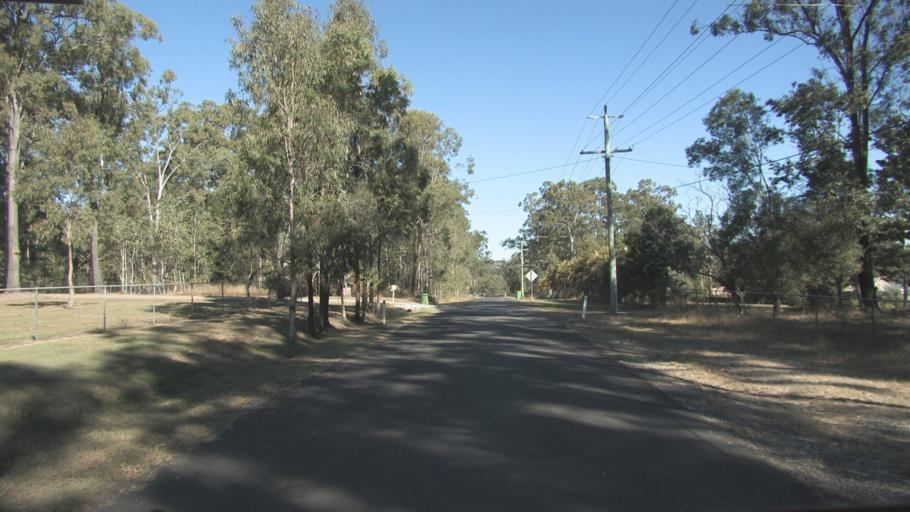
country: AU
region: Queensland
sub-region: Logan
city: Park Ridge South
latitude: -27.7297
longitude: 153.0025
